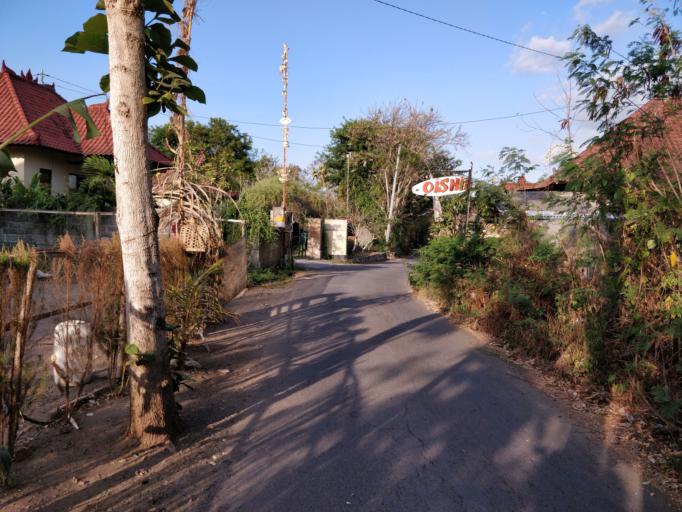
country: ID
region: Bali
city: Lembongan Kawan
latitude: -8.6858
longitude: 115.4305
